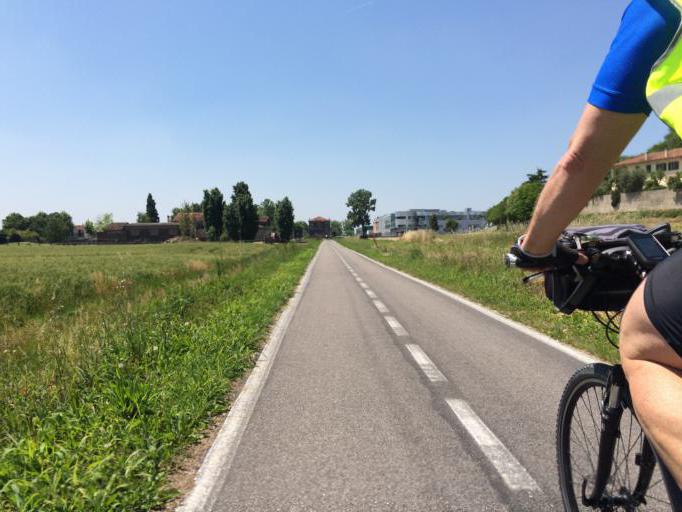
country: IT
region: Veneto
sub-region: Provincia di Vicenza
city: Ponte di Barbarano
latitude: 45.3987
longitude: 11.5681
